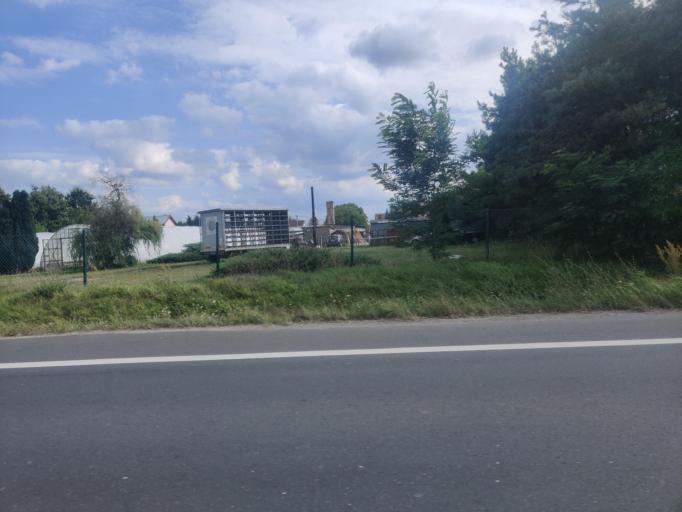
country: PL
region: Greater Poland Voivodeship
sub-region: Konin
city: Konin
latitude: 52.1914
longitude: 18.2607
